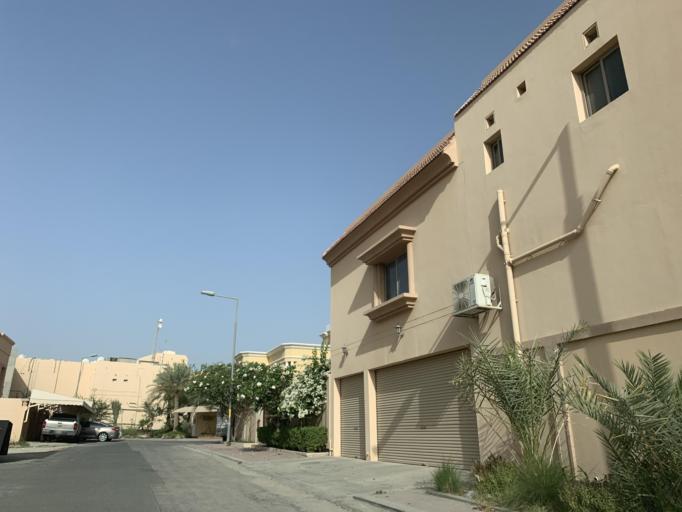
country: BH
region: Northern
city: Ar Rifa'
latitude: 26.1435
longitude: 50.5806
